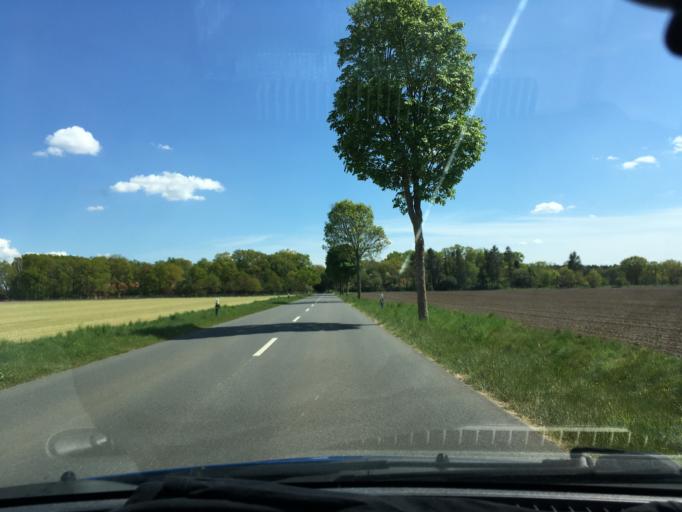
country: DE
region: Lower Saxony
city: Himbergen
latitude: 53.0880
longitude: 10.7375
